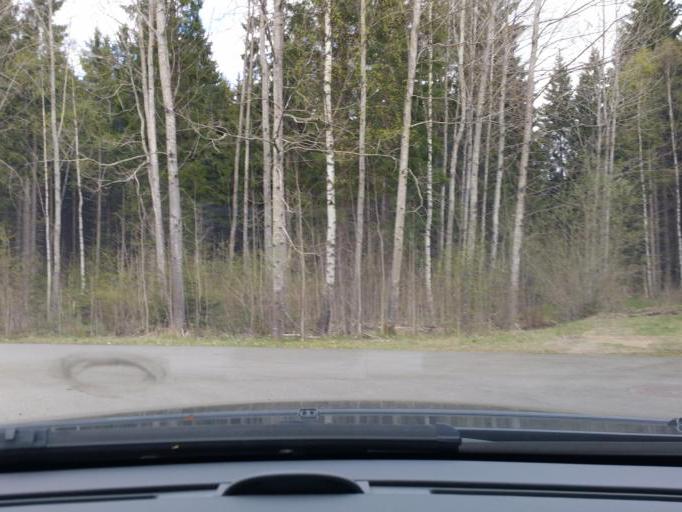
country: SE
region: Kronoberg
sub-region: Vaxjo Kommun
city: Lammhult
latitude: 57.1716
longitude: 14.6081
